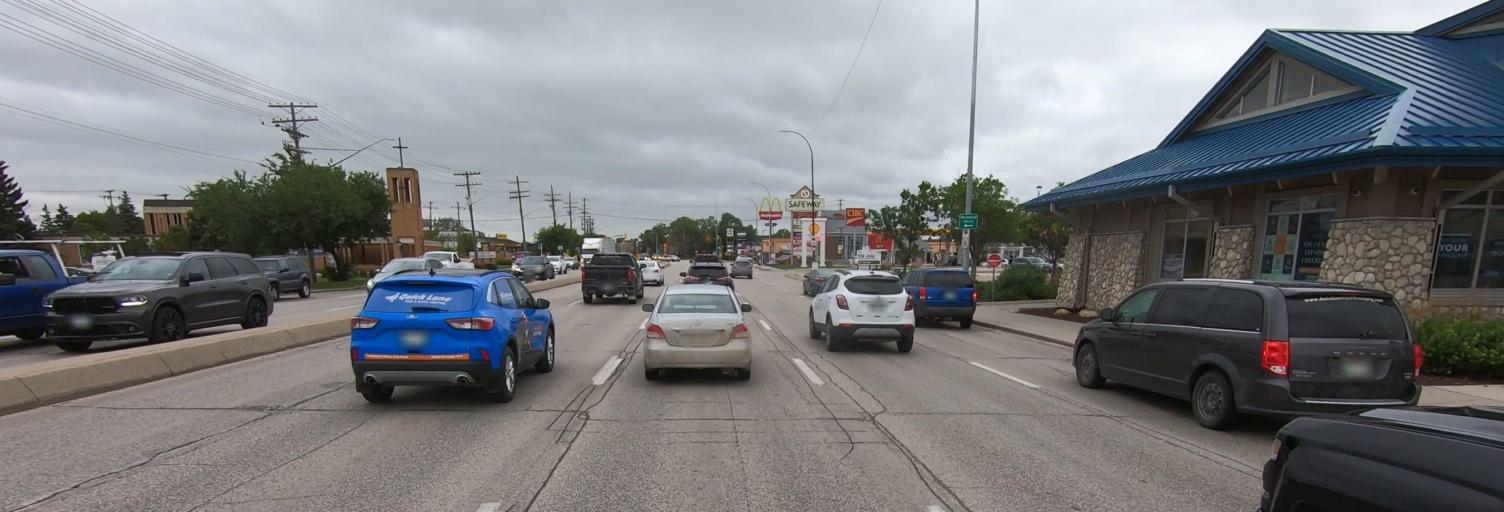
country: CA
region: Manitoba
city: Headingley
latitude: 49.8825
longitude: -97.2978
